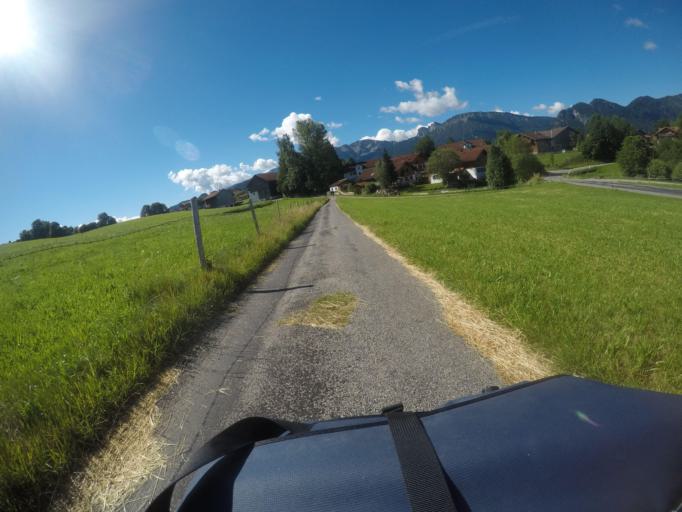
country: DE
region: Bavaria
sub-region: Swabia
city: Pfronten
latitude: 47.5988
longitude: 10.5669
